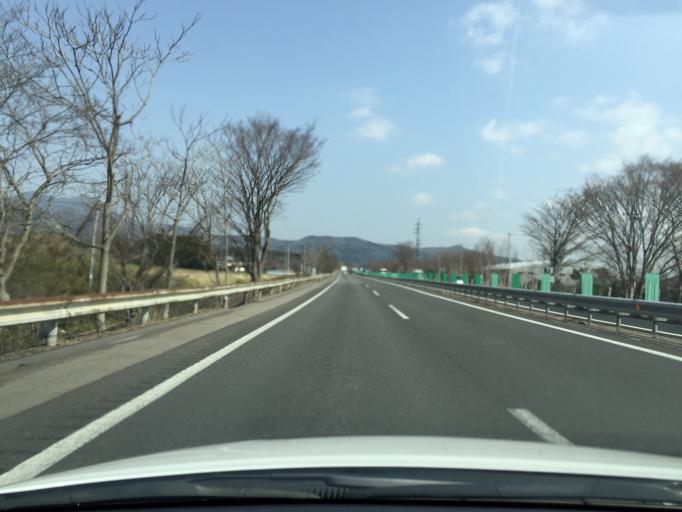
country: JP
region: Miyagi
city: Shiroishi
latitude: 38.0232
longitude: 140.6235
